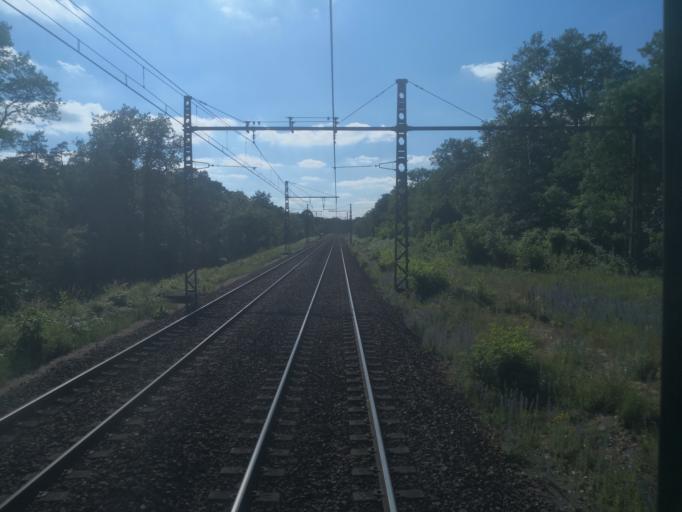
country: FR
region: Ile-de-France
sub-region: Departement de Seine-et-Marne
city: Samoreau
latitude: 48.3951
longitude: 2.7542
